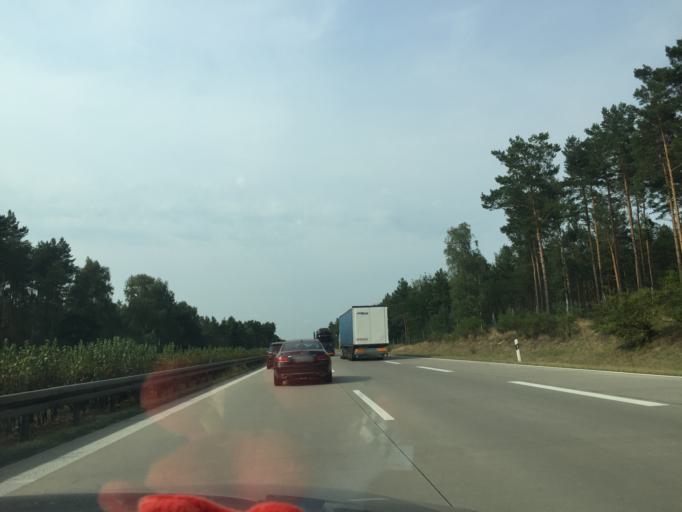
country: DE
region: Brandenburg
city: Halbe
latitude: 52.0657
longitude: 13.6524
